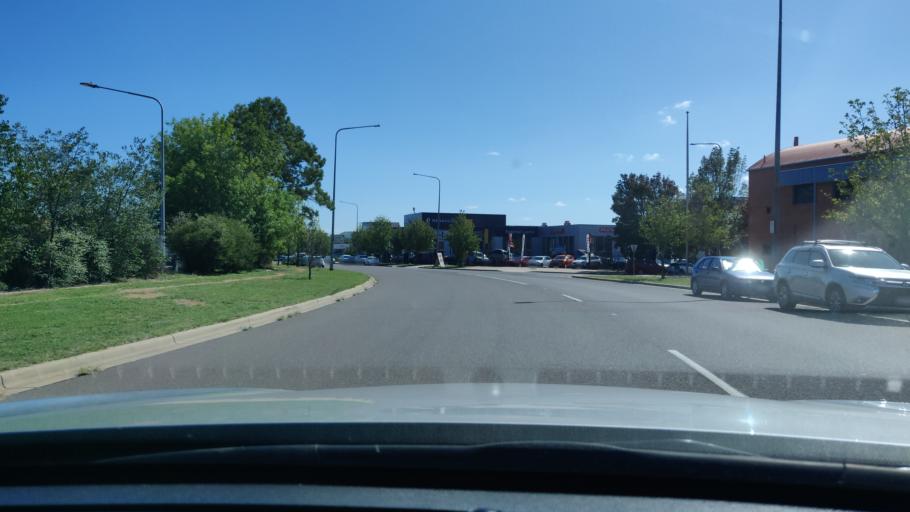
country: AU
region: Australian Capital Territory
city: Macarthur
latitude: -35.4238
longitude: 149.0704
